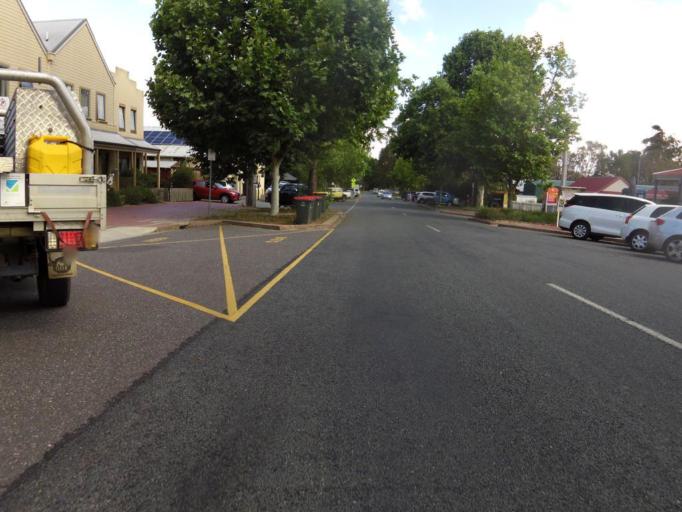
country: AU
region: Australian Capital Territory
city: Belconnen
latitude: -35.1701
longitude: 149.0698
